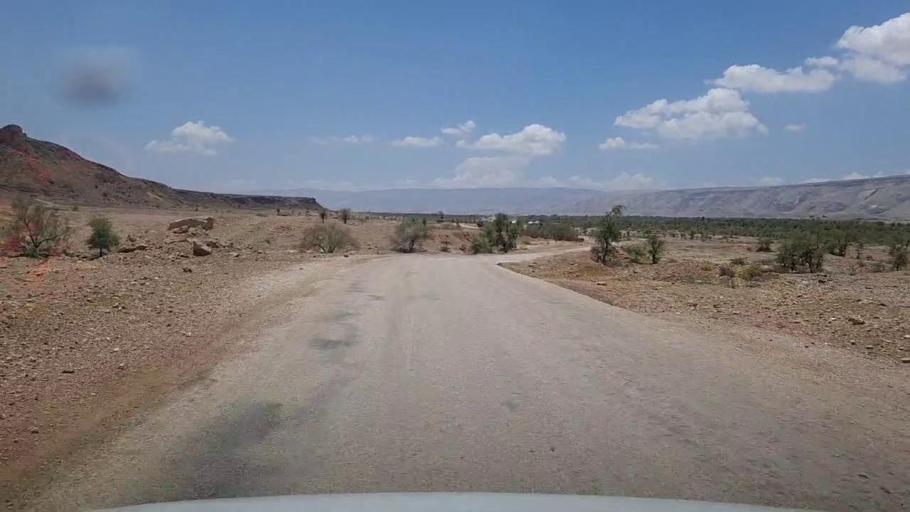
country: PK
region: Sindh
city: Bhan
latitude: 26.3014
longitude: 67.5358
